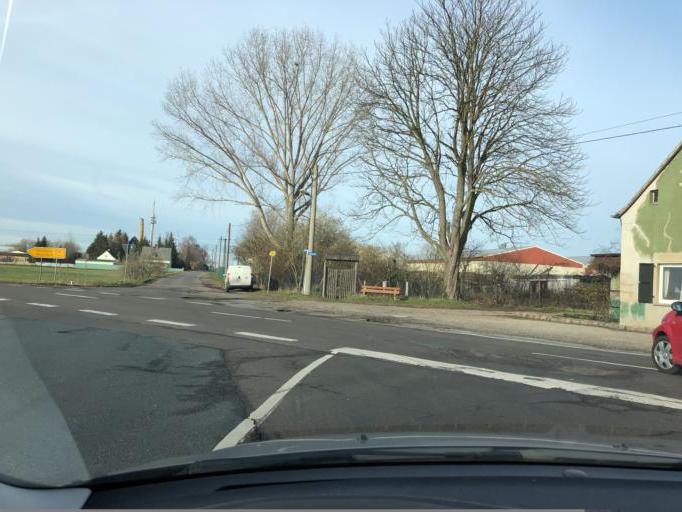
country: DE
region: Saxony-Anhalt
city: Goseck
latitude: 51.2334
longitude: 11.8856
